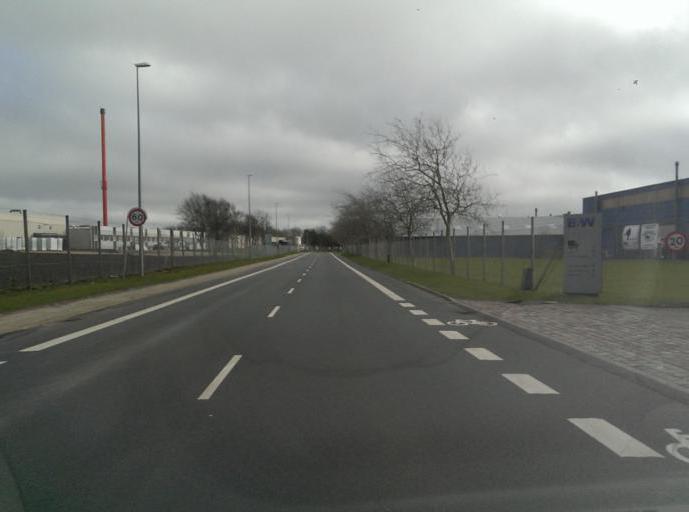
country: DK
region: South Denmark
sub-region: Esbjerg Kommune
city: Esbjerg
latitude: 55.4906
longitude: 8.4654
